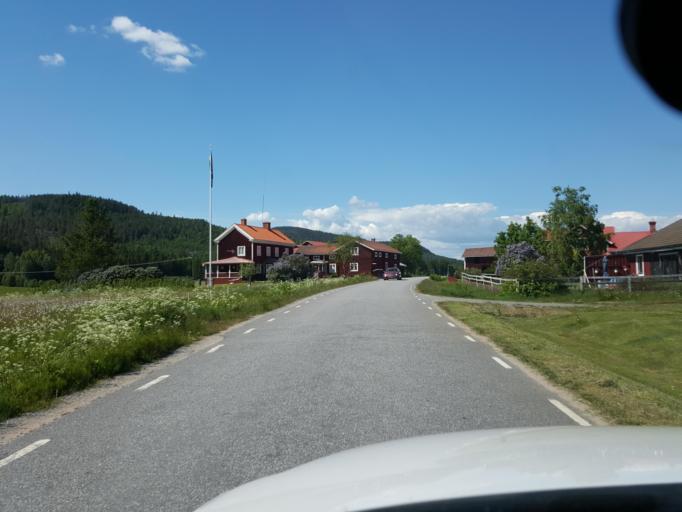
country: SE
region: Gaevleborg
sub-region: Ljusdals Kommun
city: Jaervsoe
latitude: 61.7141
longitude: 16.2965
